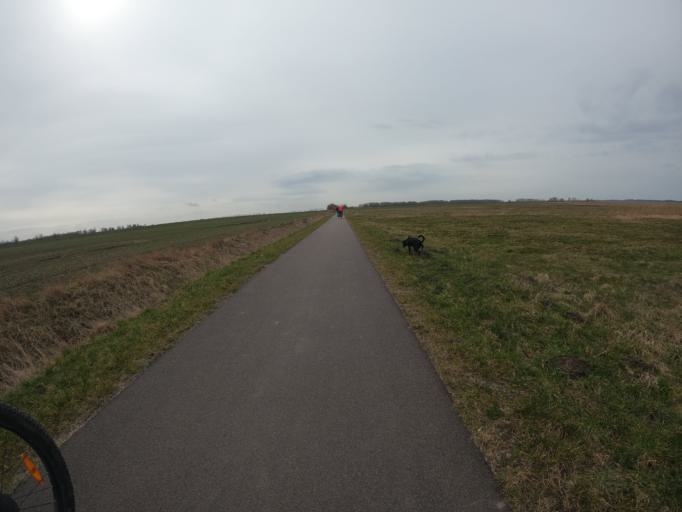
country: PL
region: West Pomeranian Voivodeship
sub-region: Powiat gryficki
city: Mrzezyno
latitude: 54.1181
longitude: 15.3053
